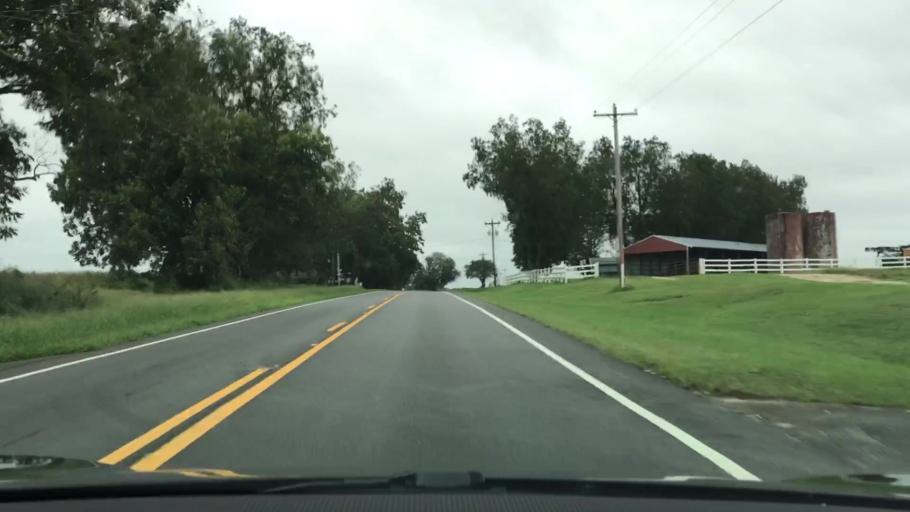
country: US
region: Alabama
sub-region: Covington County
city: Opp
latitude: 31.2343
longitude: -86.1620
